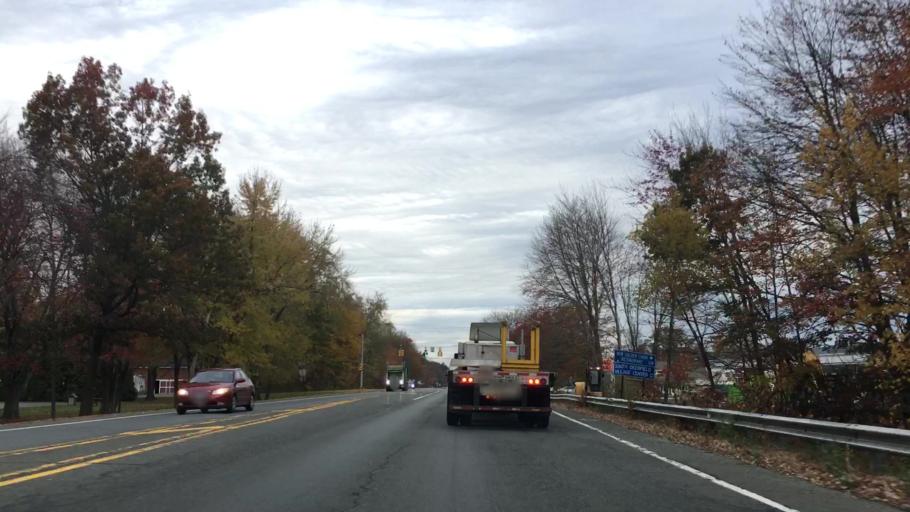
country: US
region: Massachusetts
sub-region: Franklin County
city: South Deerfield
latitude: 42.4761
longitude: -72.6137
